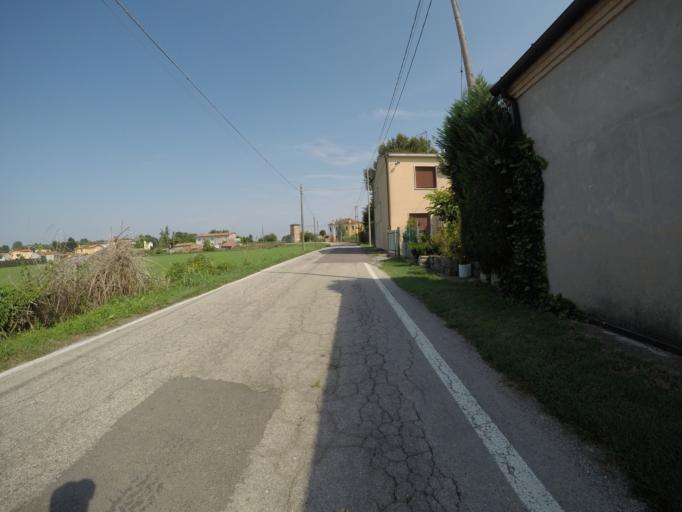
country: IT
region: Veneto
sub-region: Provincia di Rovigo
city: Lendinara
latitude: 45.0706
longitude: 11.6158
